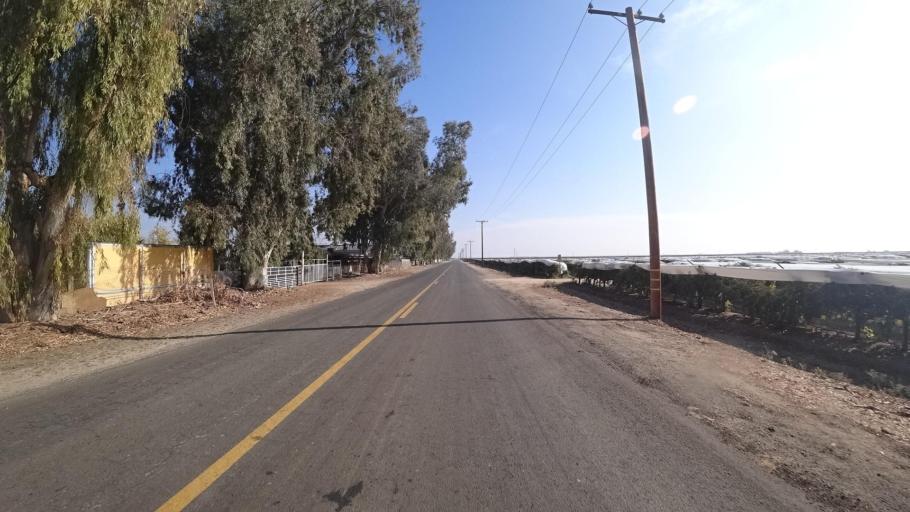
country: US
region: California
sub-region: Kern County
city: McFarland
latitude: 35.6892
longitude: -119.1938
